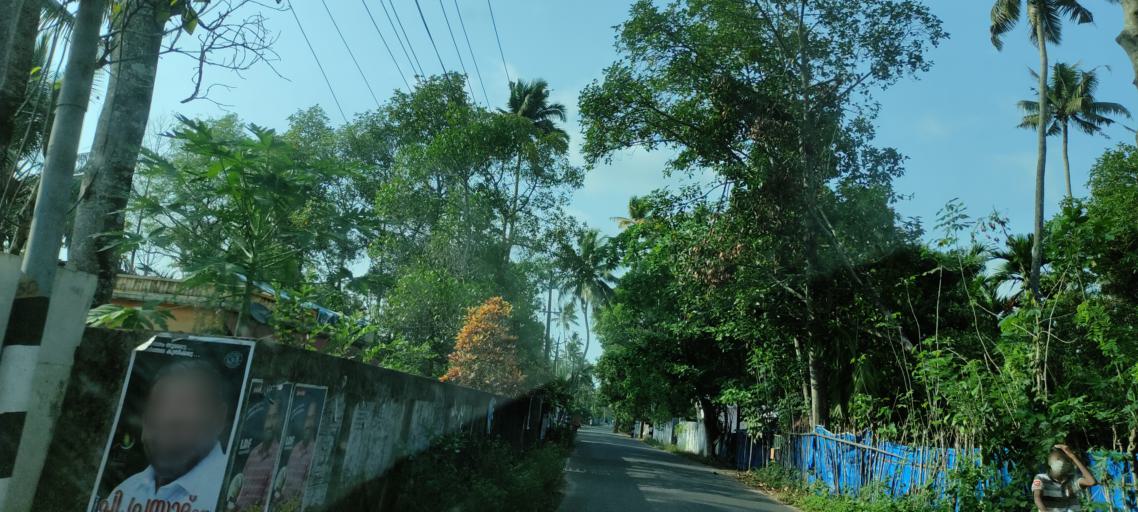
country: IN
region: Kerala
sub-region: Alappuzha
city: Vayalar
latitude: 9.6921
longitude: 76.2906
